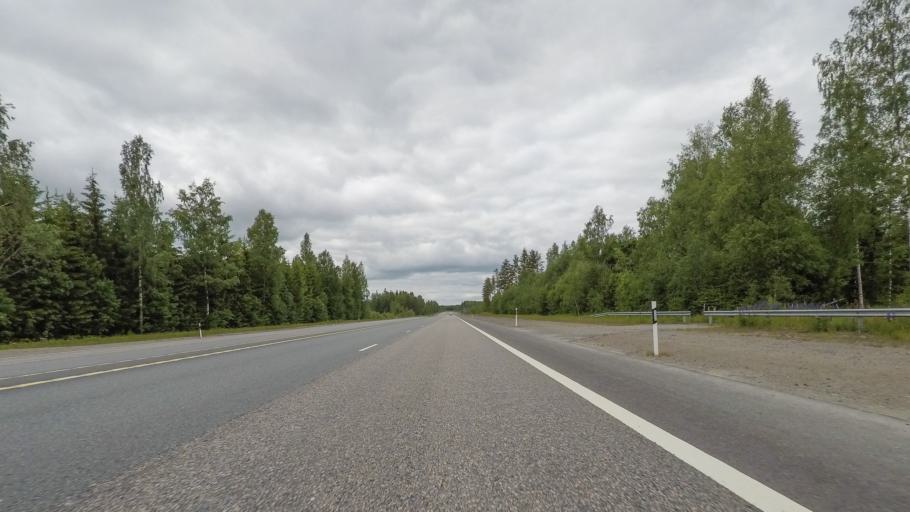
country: FI
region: Central Finland
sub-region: Joutsa
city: Joutsa
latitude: 61.7679
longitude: 26.1027
